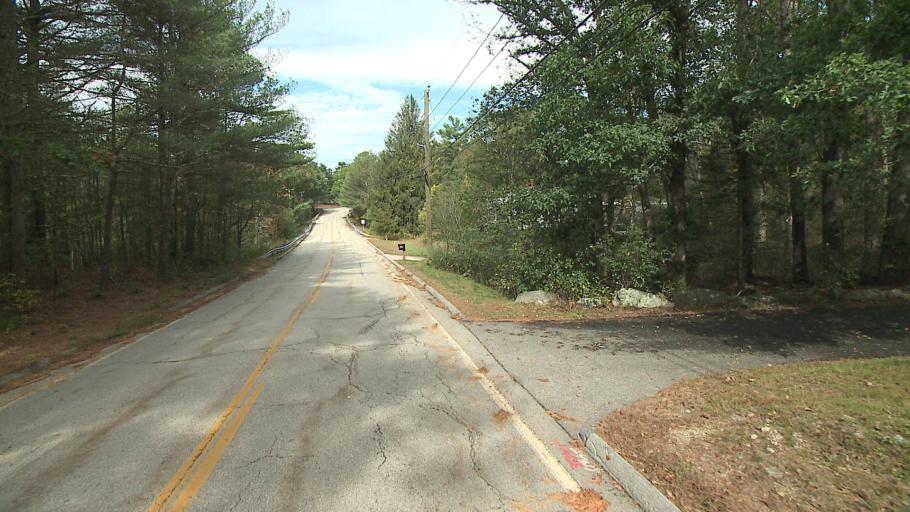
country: US
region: Connecticut
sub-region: Windham County
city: Thompson
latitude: 41.9278
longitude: -71.8223
